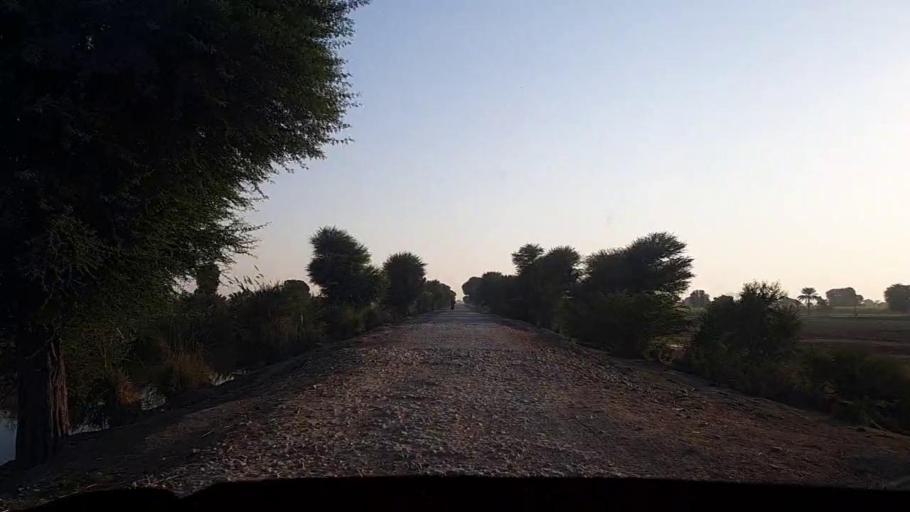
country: PK
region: Sindh
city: Sobhadero
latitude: 27.3789
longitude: 68.3803
